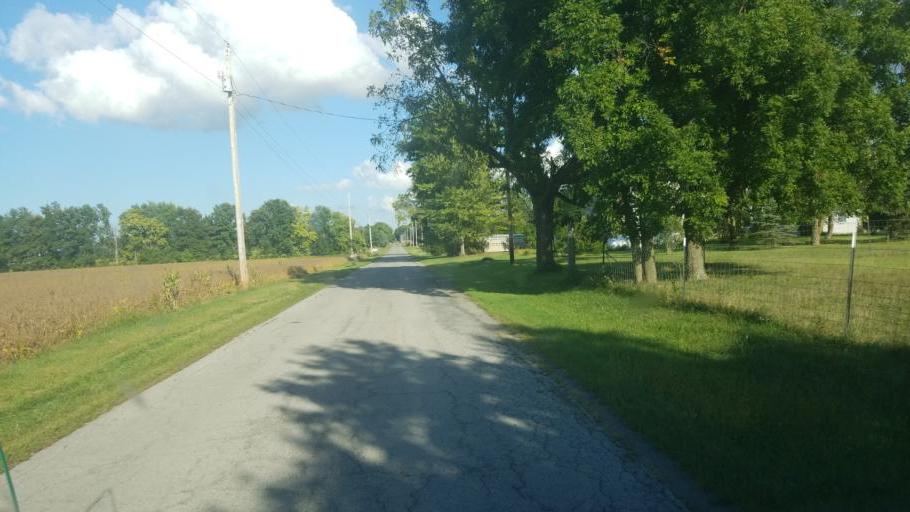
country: US
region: Ohio
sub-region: Hancock County
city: Arlington
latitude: 40.9360
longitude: -83.6912
